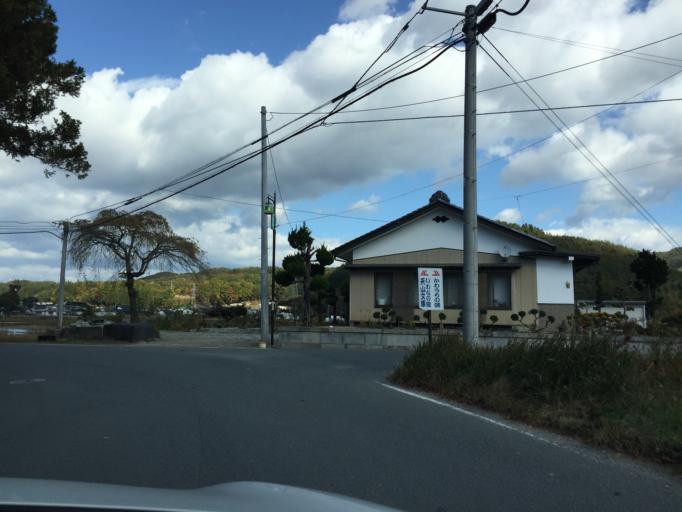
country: JP
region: Fukushima
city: Namie
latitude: 37.3371
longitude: 140.8044
